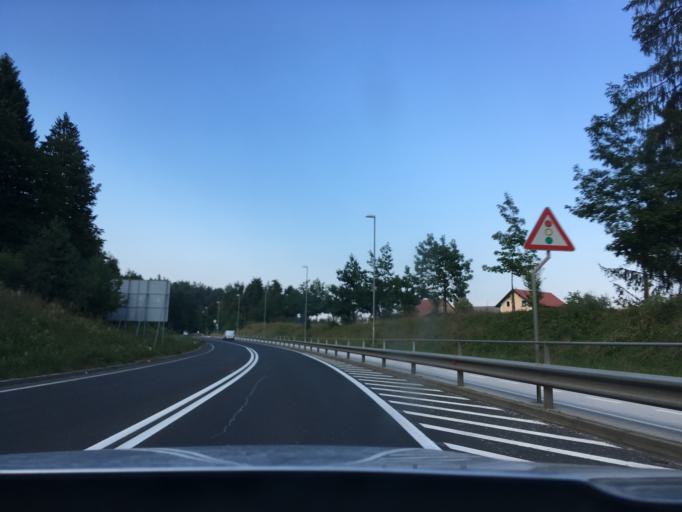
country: SI
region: Novo Mesto
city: Novo Mesto
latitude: 45.8223
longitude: 15.1729
